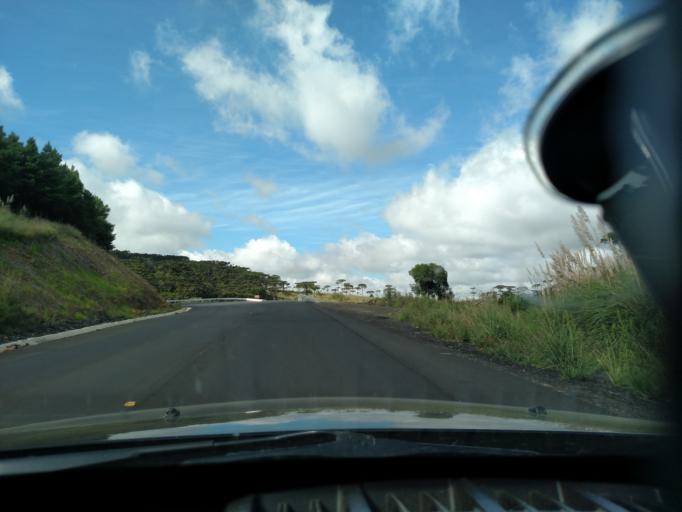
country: BR
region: Santa Catarina
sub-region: Lages
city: Lages
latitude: -27.9655
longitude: -50.0989
